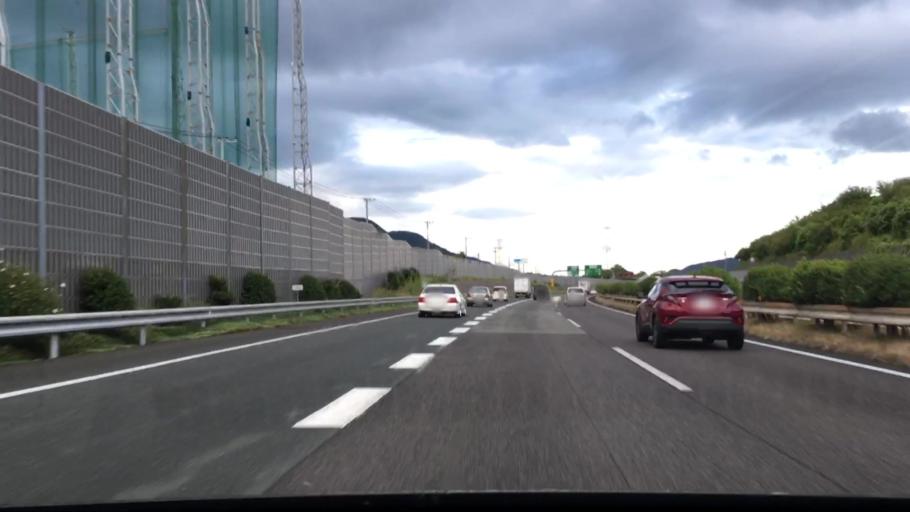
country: JP
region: Fukuoka
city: Kitakyushu
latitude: 33.8297
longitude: 130.9012
